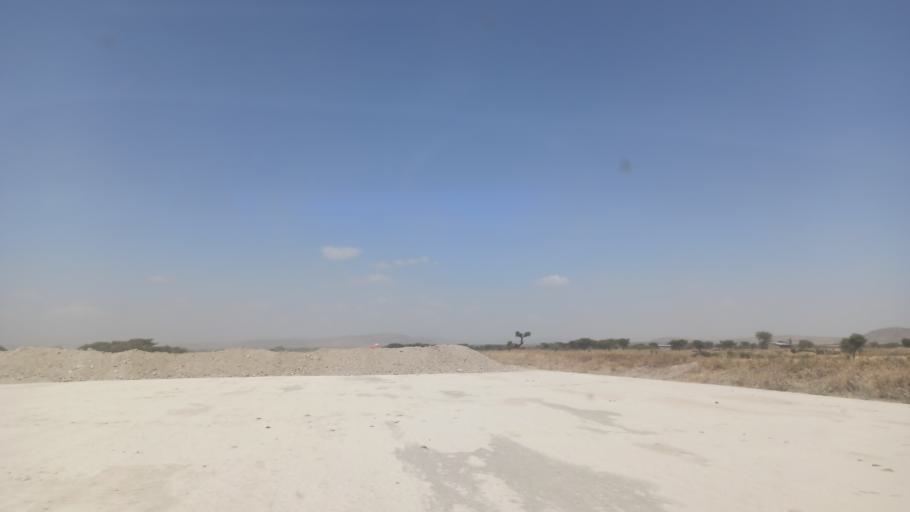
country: ET
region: Oromiya
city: Ziway
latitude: 7.7335
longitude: 38.6241
